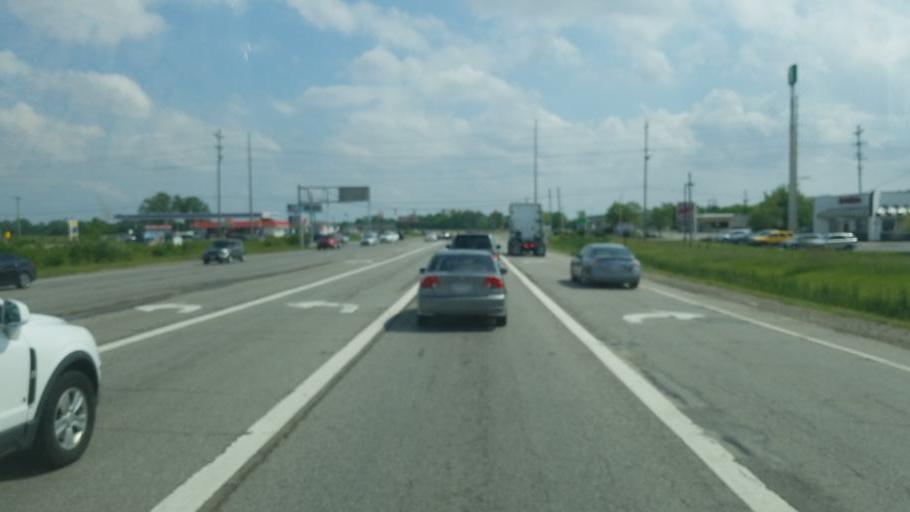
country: US
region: Ohio
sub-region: Franklin County
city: Lincoln Village
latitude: 39.9744
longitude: -83.1502
